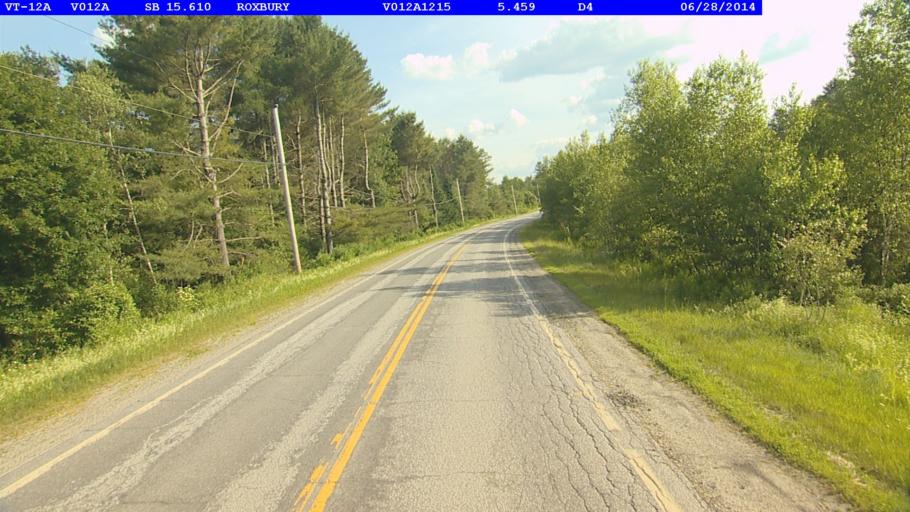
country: US
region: Vermont
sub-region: Washington County
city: Northfield
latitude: 44.1037
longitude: -72.7296
